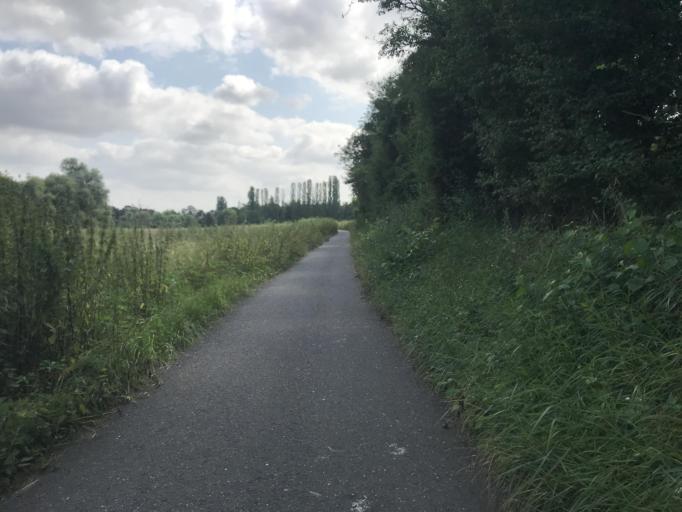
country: DE
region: Hesse
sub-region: Regierungsbezirk Darmstadt
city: Hochheim am Main
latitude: 50.0176
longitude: 8.3288
